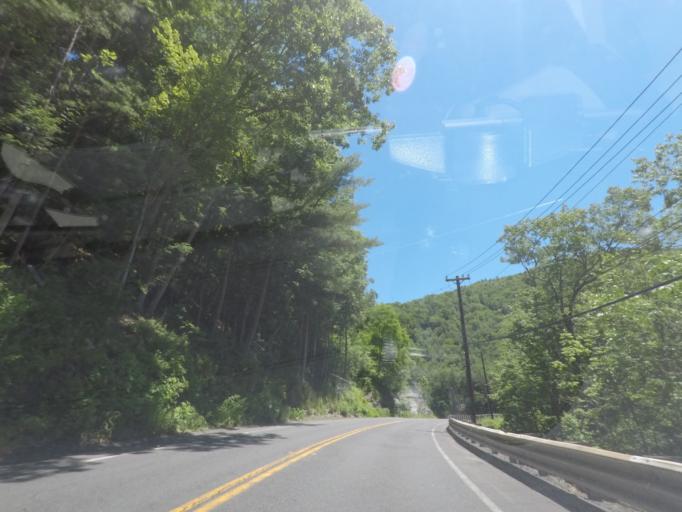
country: US
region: Massachusetts
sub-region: Berkshire County
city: Becket
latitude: 42.2741
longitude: -72.9976
